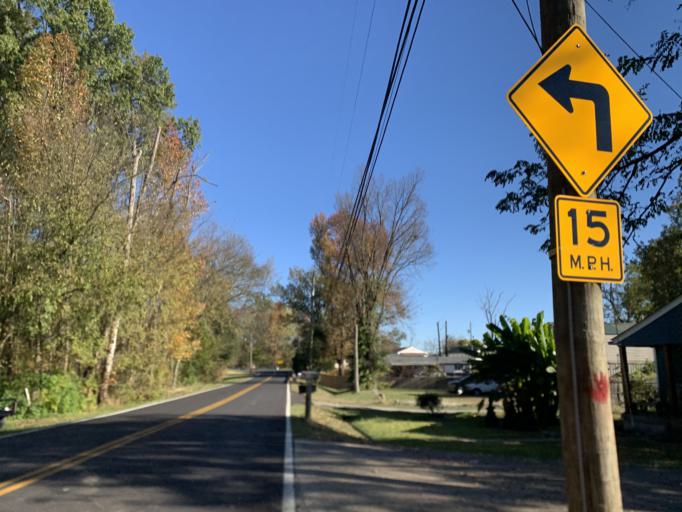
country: US
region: Kentucky
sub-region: Jefferson County
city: Pleasure Ridge Park
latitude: 38.1562
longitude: -85.8714
